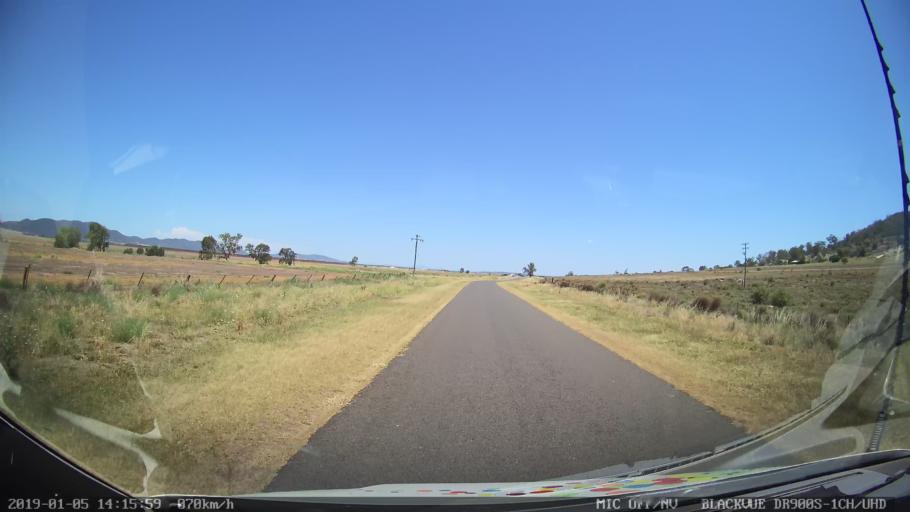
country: AU
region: New South Wales
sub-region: Liverpool Plains
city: Quirindi
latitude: -31.2523
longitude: 150.4721
